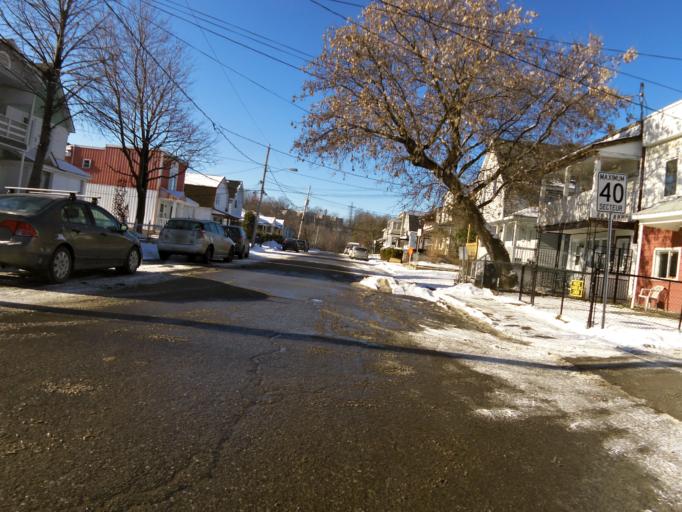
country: CA
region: Ontario
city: Ottawa
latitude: 45.4259
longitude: -75.7339
